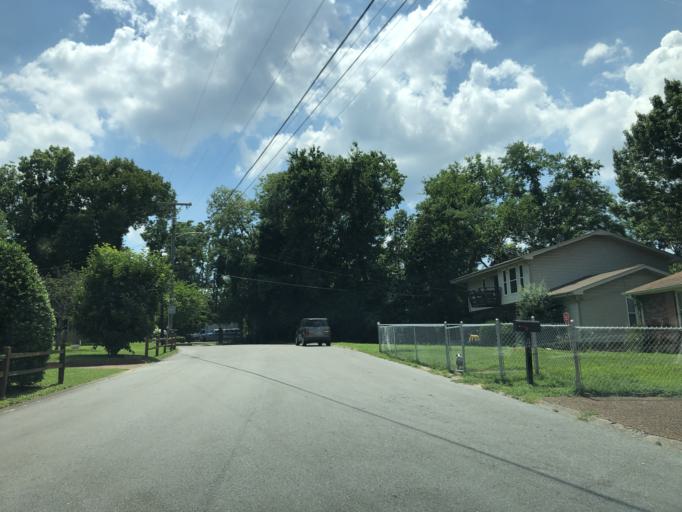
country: US
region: Tennessee
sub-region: Davidson County
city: Oak Hill
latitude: 36.1250
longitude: -86.7235
